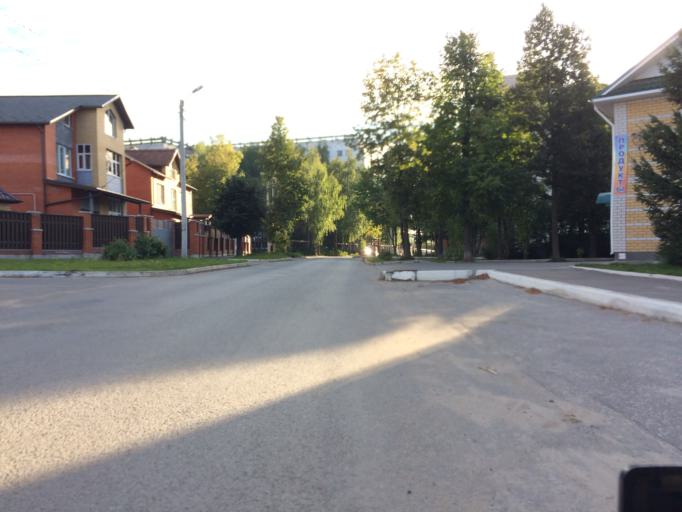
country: RU
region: Mariy-El
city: Yoshkar-Ola
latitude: 56.6517
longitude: 47.9736
